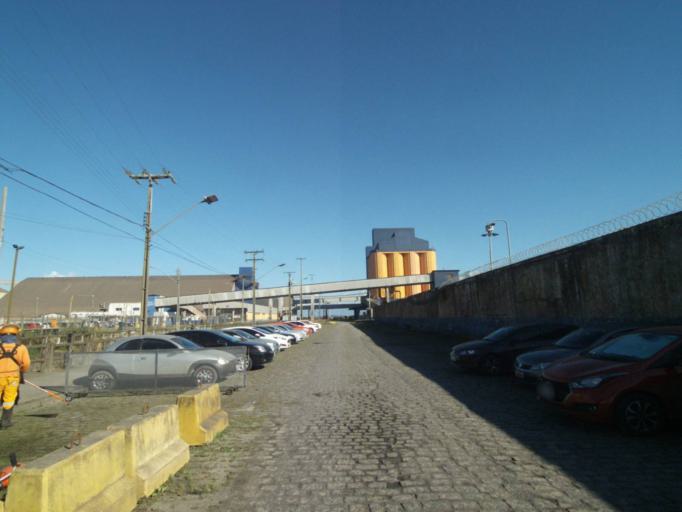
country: BR
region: Parana
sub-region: Paranagua
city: Paranagua
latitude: -25.5033
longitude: -48.5230
